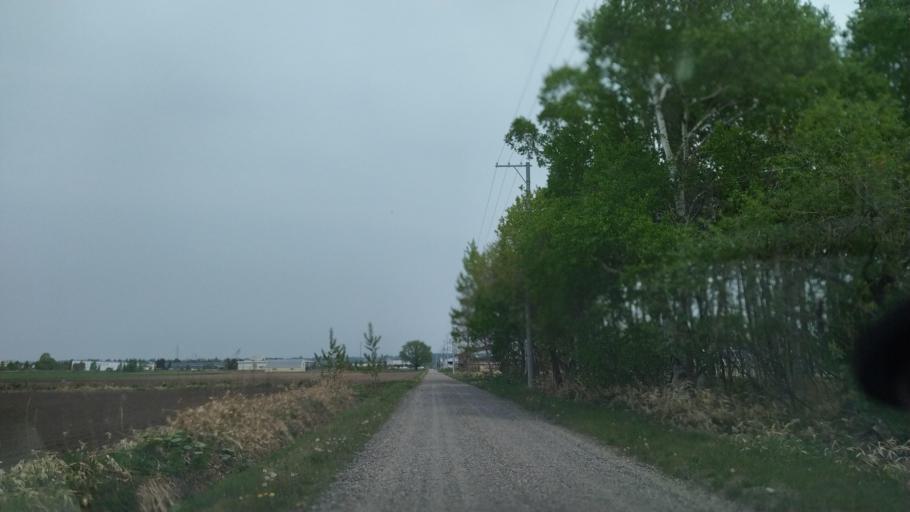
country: JP
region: Hokkaido
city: Obihiro
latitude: 42.9162
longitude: 143.0969
